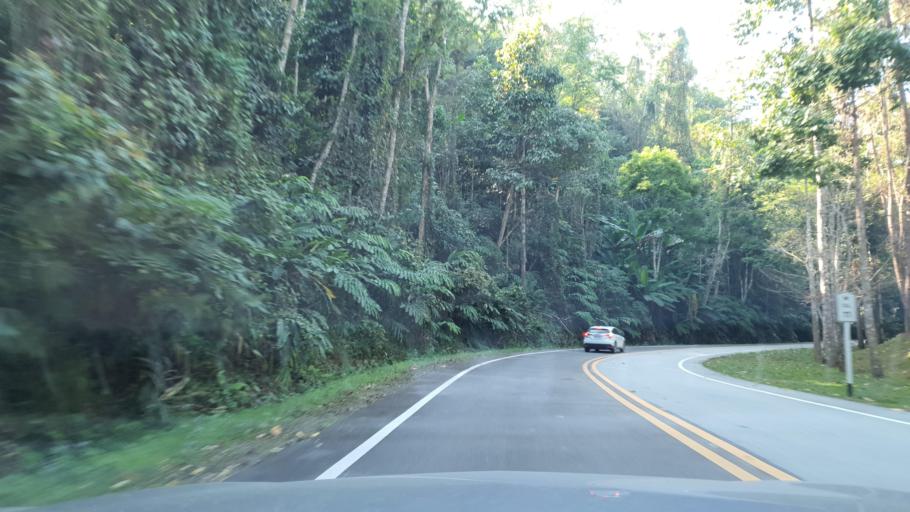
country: TH
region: Chiang Rai
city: Mae Lao
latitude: 19.8748
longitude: 99.6271
